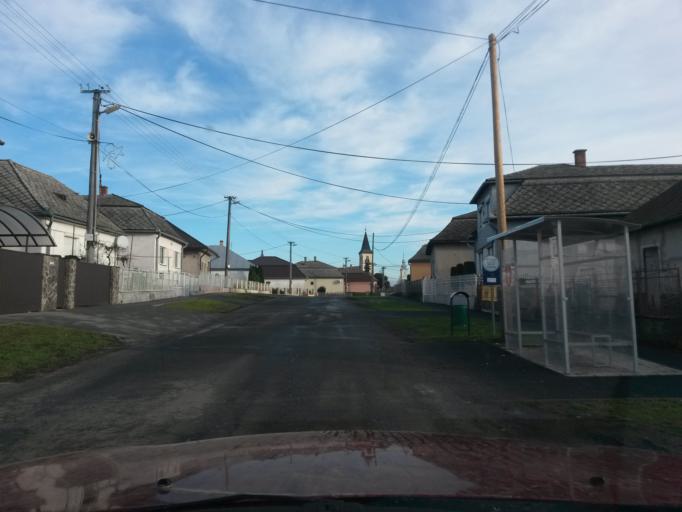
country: SK
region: Kosicky
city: Cierna nad Tisou
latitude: 48.5398
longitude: 22.0202
